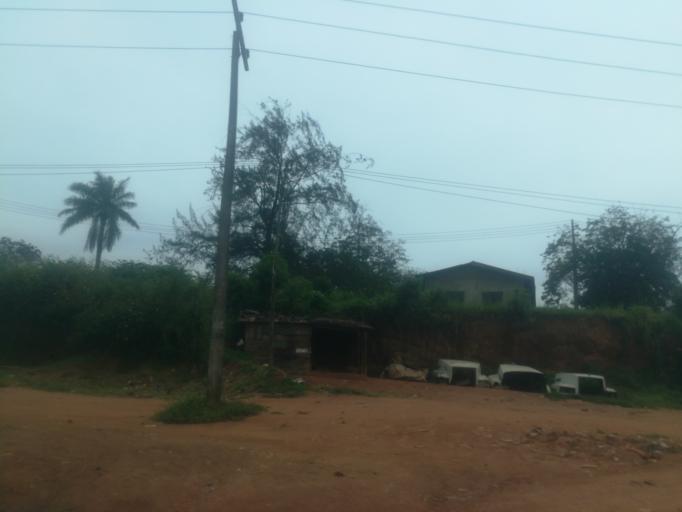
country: NG
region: Oyo
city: Ibadan
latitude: 7.3547
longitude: 3.9212
